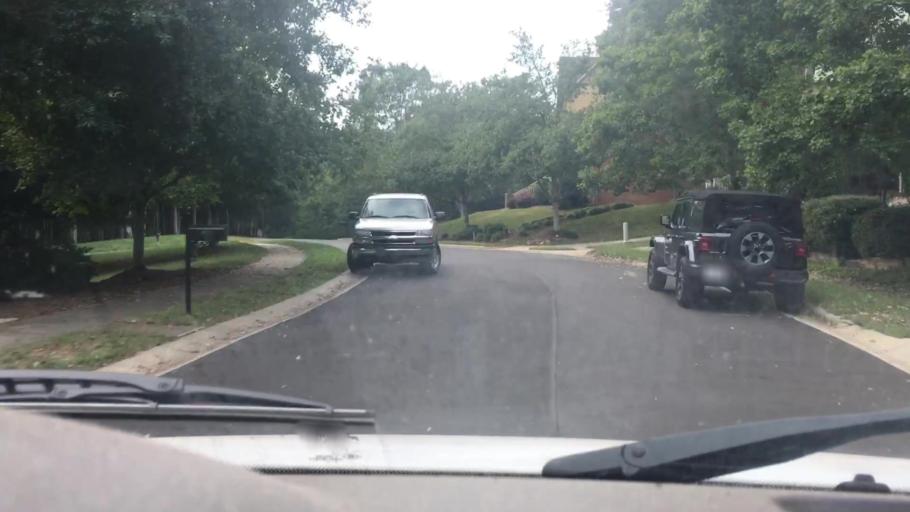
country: US
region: North Carolina
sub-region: Gaston County
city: Davidson
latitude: 35.4902
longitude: -80.8237
